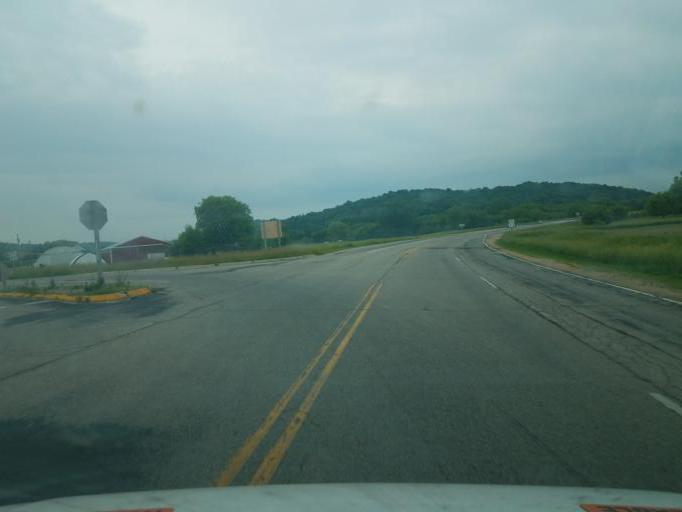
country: US
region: Wisconsin
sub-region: Vernon County
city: Hillsboro
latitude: 43.6566
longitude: -90.3904
